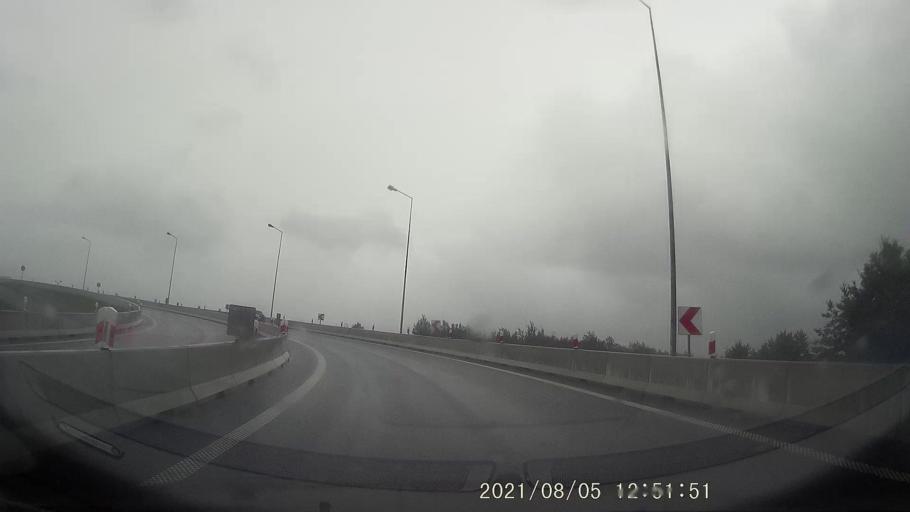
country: PL
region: Opole Voivodeship
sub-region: Powiat krapkowicki
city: Gogolin
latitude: 50.4883
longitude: 17.9944
